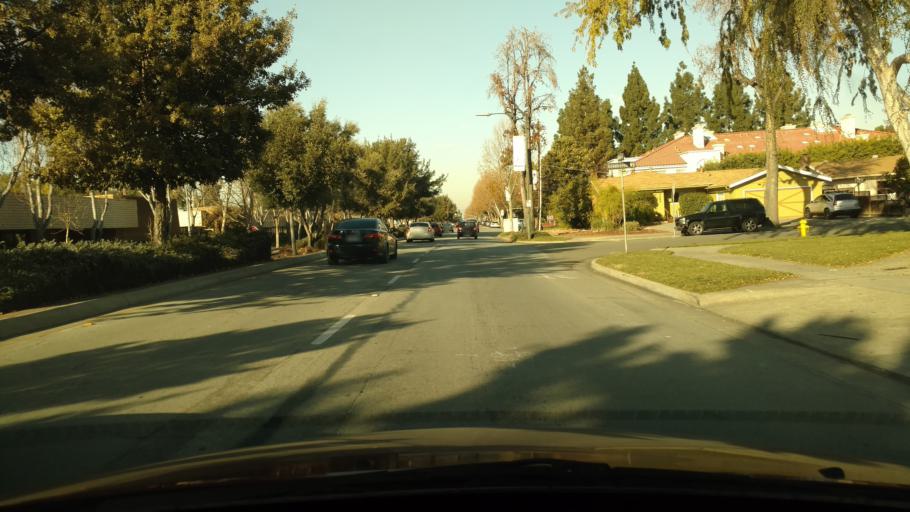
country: US
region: California
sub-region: Santa Clara County
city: Campbell
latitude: 37.3055
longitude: -121.9499
